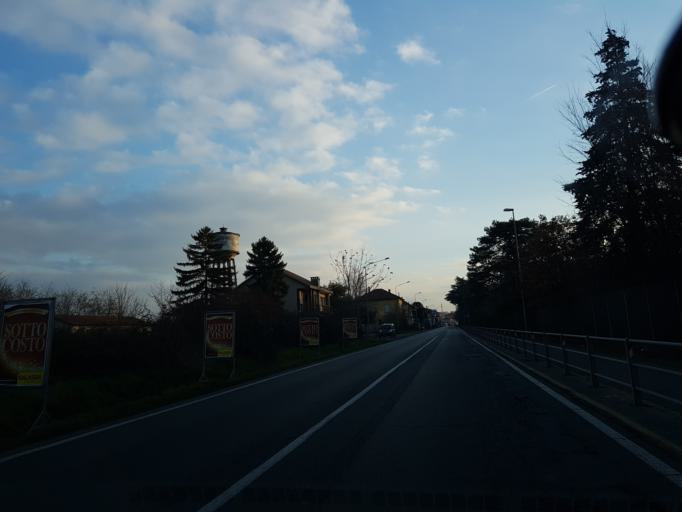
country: IT
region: Piedmont
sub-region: Provincia di Alessandria
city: Novi Ligure
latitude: 44.7778
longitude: 8.7894
